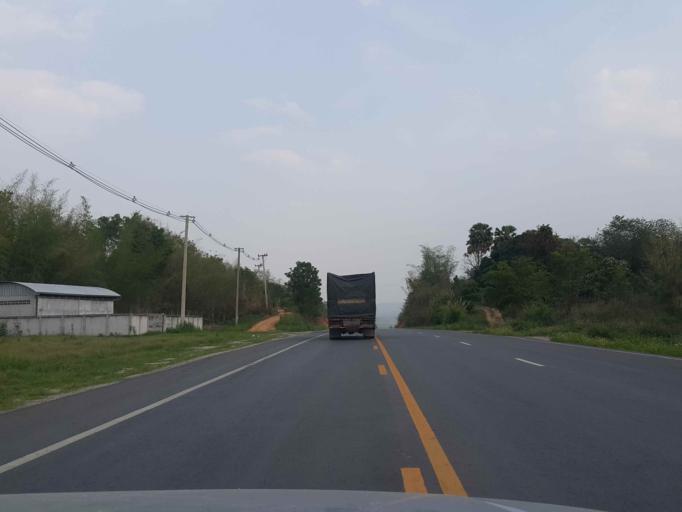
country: TH
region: Chiang Mai
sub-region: Amphoe Chiang Dao
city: Chiang Dao
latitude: 19.3654
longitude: 98.9508
